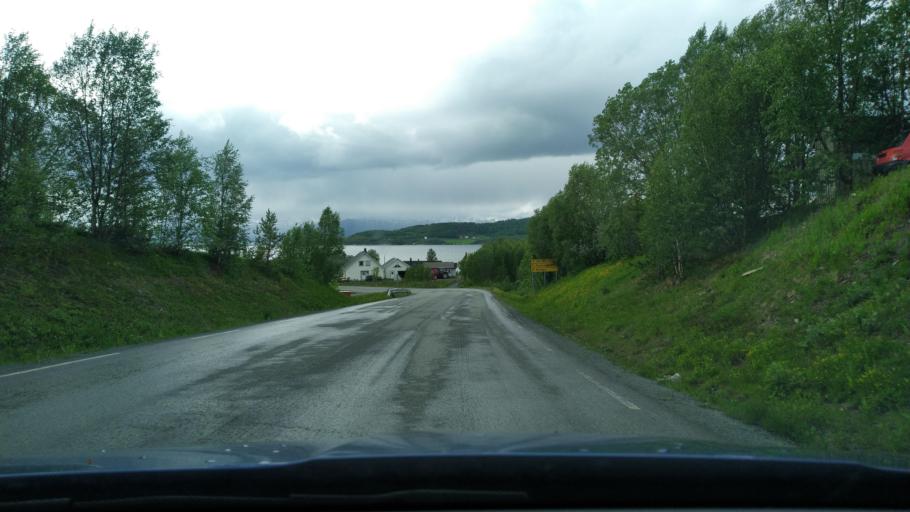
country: NO
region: Troms
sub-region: Dyroy
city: Brostadbotn
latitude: 69.0823
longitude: 17.6942
